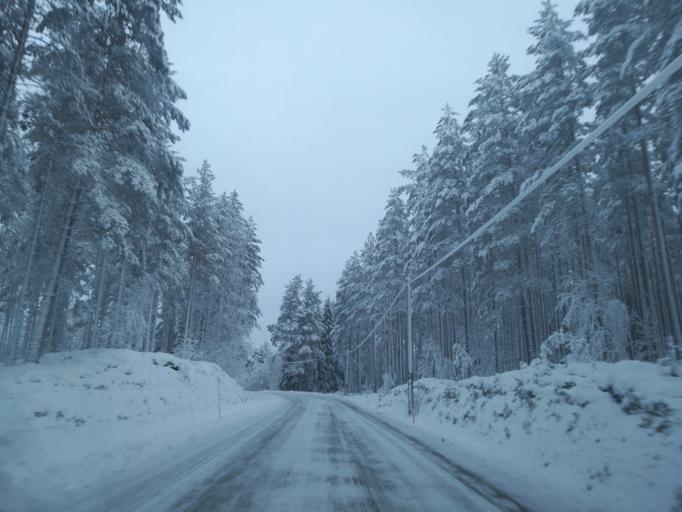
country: NO
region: Hedmark
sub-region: Grue
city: Kirkenaer
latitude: 60.5005
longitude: 12.5595
